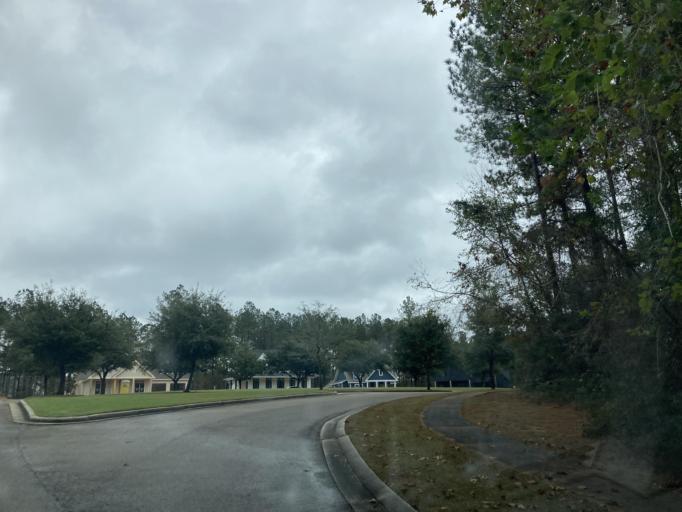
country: US
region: Mississippi
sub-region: Lamar County
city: West Hattiesburg
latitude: 31.2876
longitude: -89.4753
